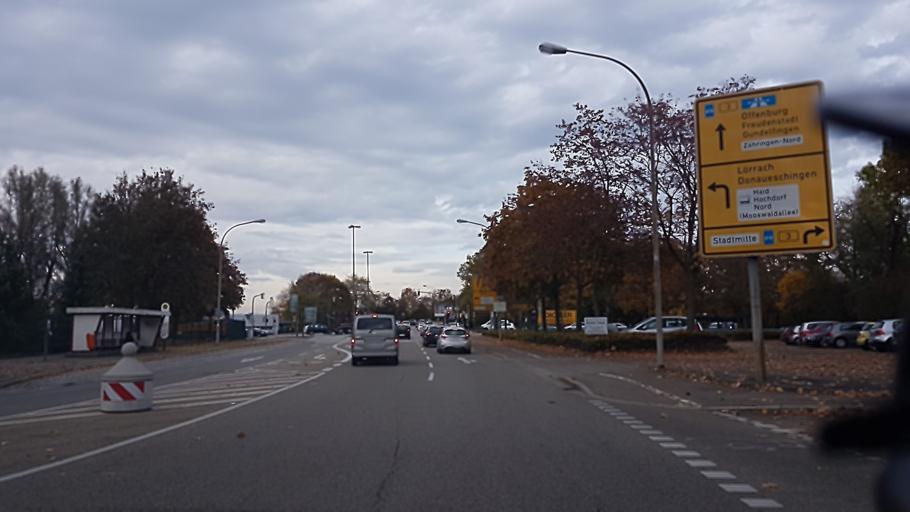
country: DE
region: Baden-Wuerttemberg
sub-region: Freiburg Region
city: Gundelfingen
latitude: 48.0326
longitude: 7.8604
